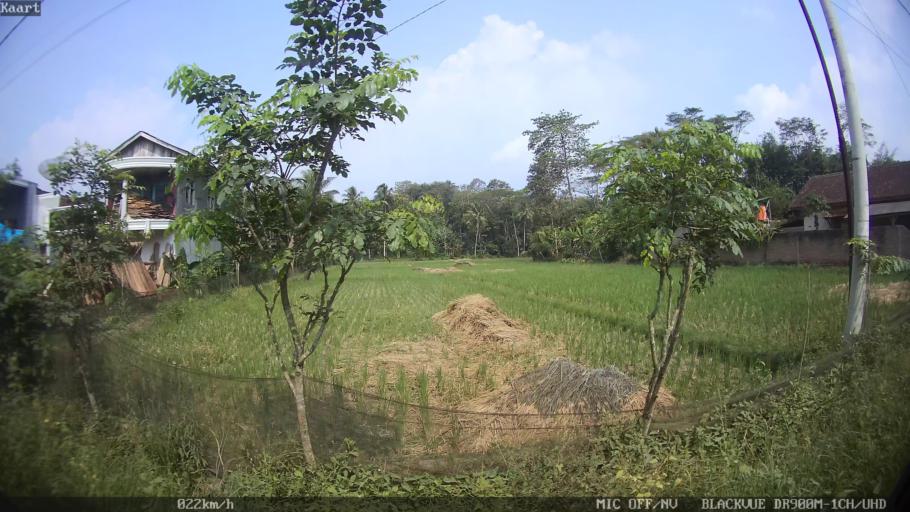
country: ID
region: Lampung
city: Pringsewu
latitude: -5.3937
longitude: 104.9926
